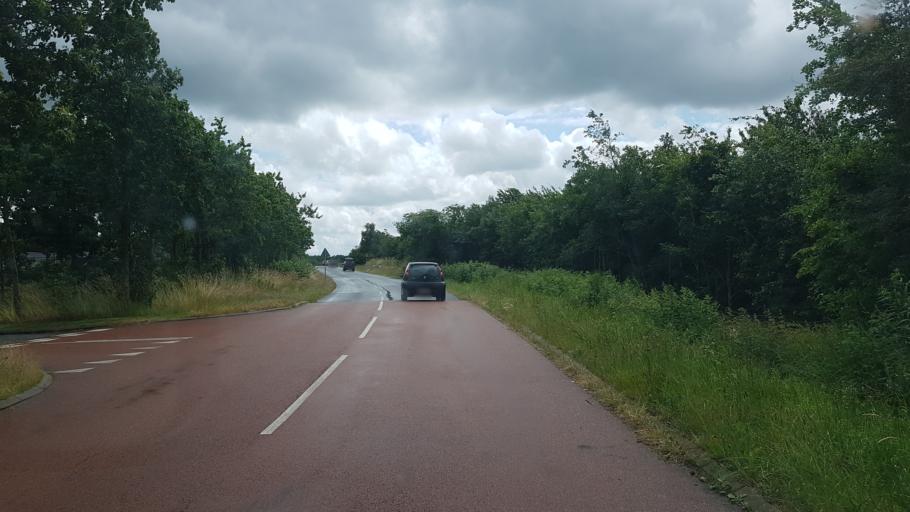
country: DK
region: South Denmark
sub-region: Kolding Kommune
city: Lunderskov
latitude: 55.4708
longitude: 9.2896
